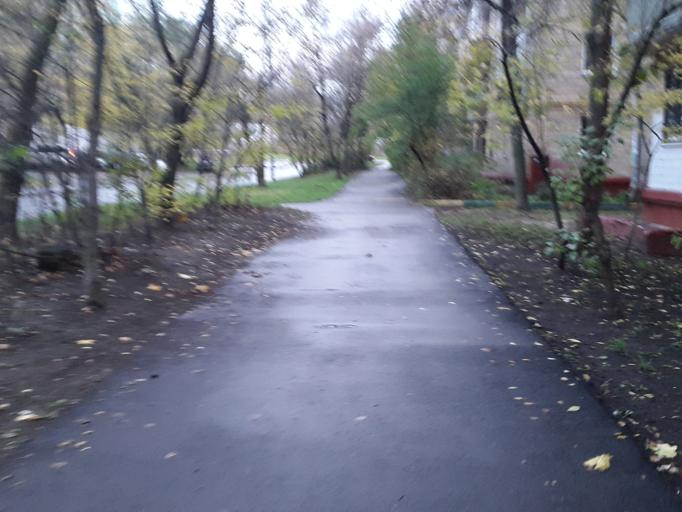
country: RU
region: Moscow
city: Pokrovskoye-Streshnevo
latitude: 55.8126
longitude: 37.4555
